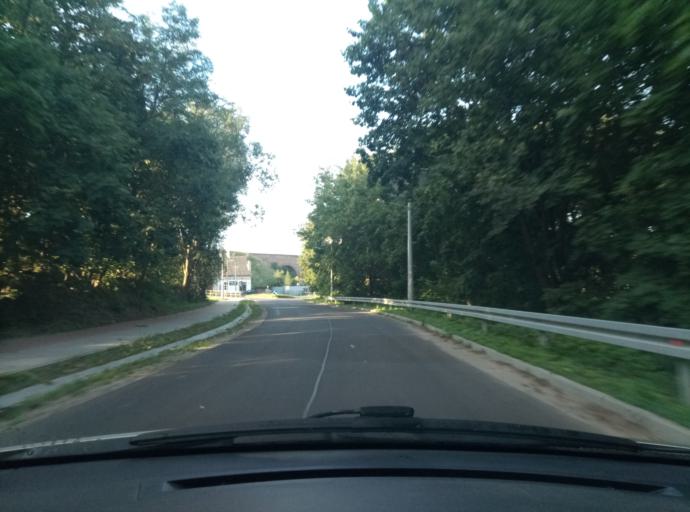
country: PL
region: Kujawsko-Pomorskie
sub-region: Powiat brodnicki
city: Jablonowo Pomorskie
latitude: 53.3881
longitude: 19.1428
